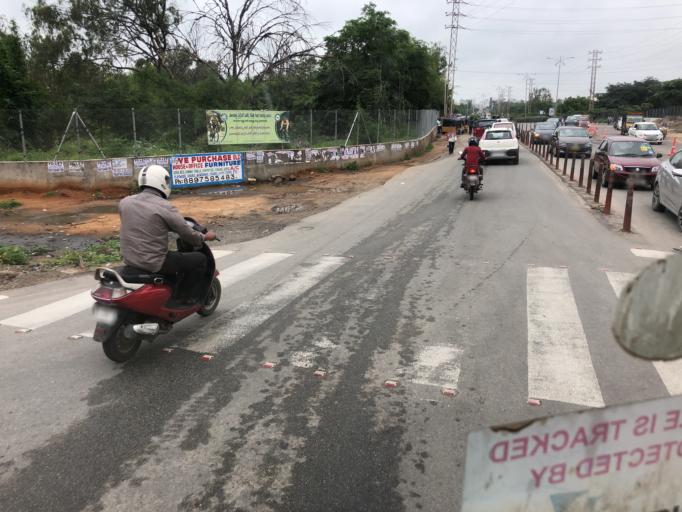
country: IN
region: Telangana
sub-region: Rangareddi
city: Kukatpalli
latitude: 17.4554
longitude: 78.3639
